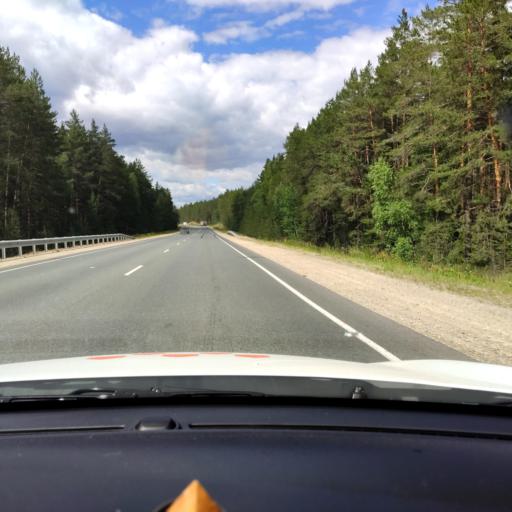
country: RU
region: Mariy-El
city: Pomary
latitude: 56.0566
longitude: 48.3724
